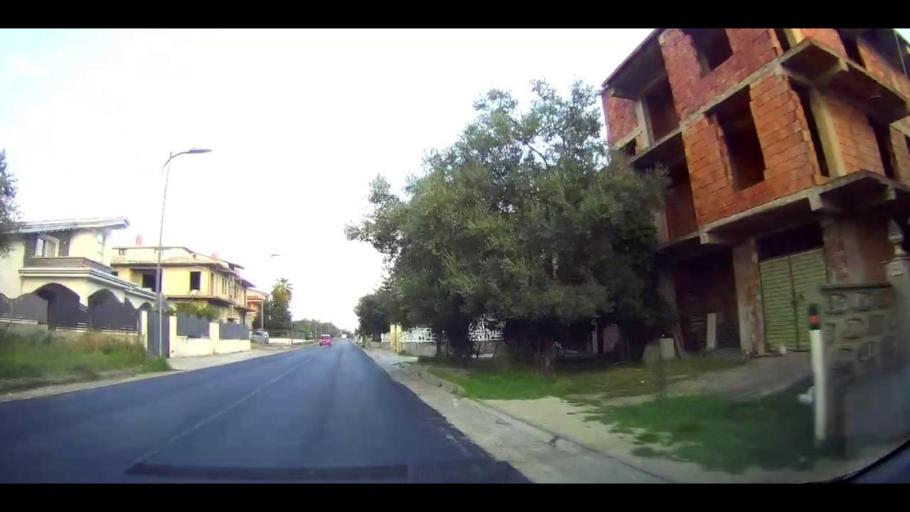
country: IT
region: Calabria
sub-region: Provincia di Crotone
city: Torretta
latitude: 39.4576
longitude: 17.0320
